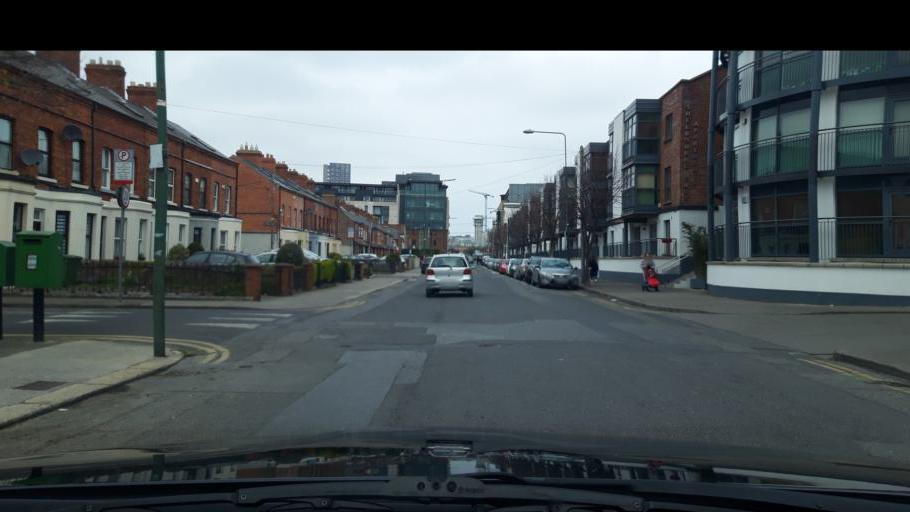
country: IE
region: Leinster
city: Ringsend
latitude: 53.3399
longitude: -6.2324
